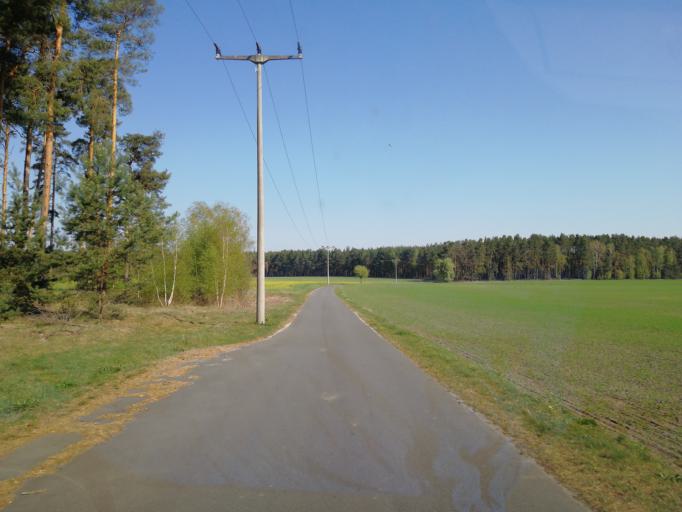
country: DE
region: Brandenburg
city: Bronkow
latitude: 51.6528
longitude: 13.8556
